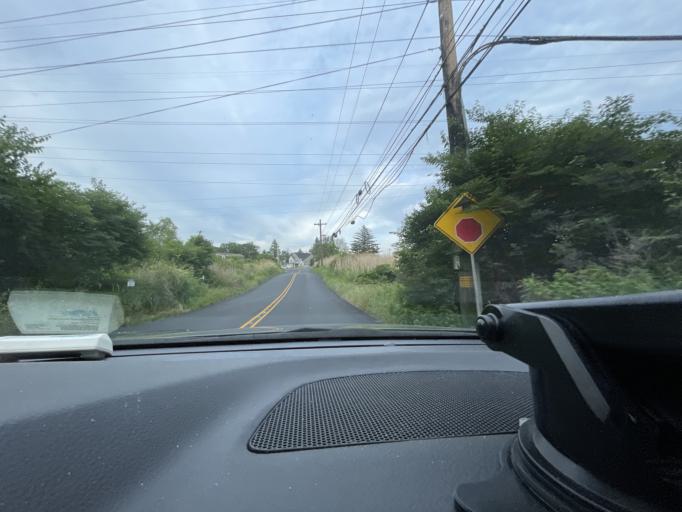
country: US
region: Pennsylvania
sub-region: Montgomery County
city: Plymouth Meeting
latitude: 40.1159
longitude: -75.2999
